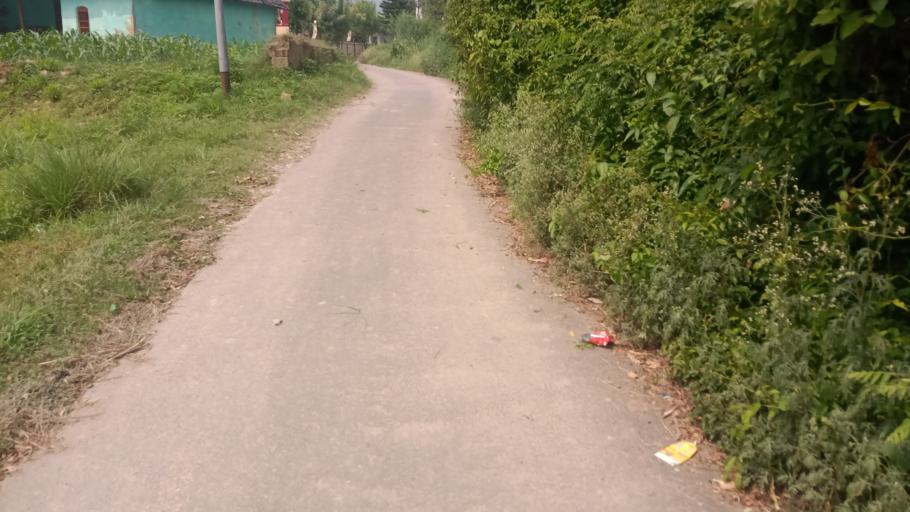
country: IN
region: Himachal Pradesh
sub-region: Hamirpur
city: Nadaun
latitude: 31.6928
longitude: 76.3574
